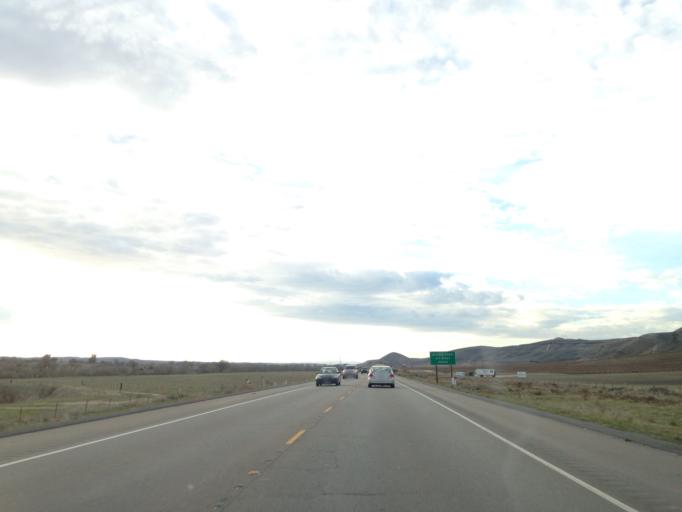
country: US
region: California
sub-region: San Luis Obispo County
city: Shandon
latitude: 35.6624
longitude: -120.3733
